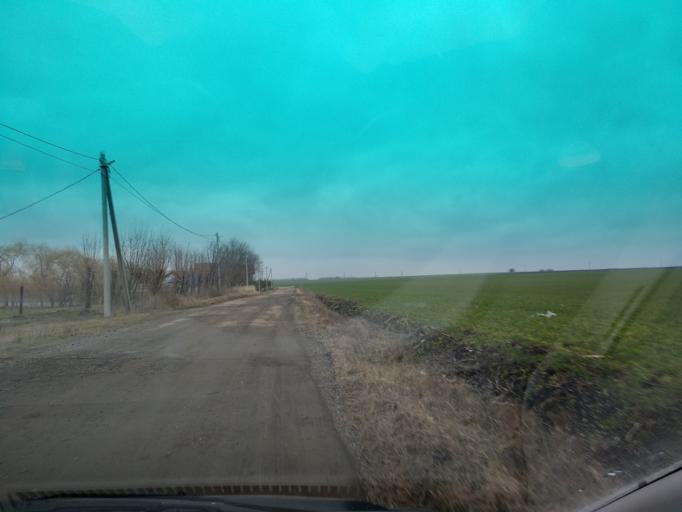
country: RU
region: Krasnodarskiy
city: Vyselki
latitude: 45.6636
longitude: 39.7018
